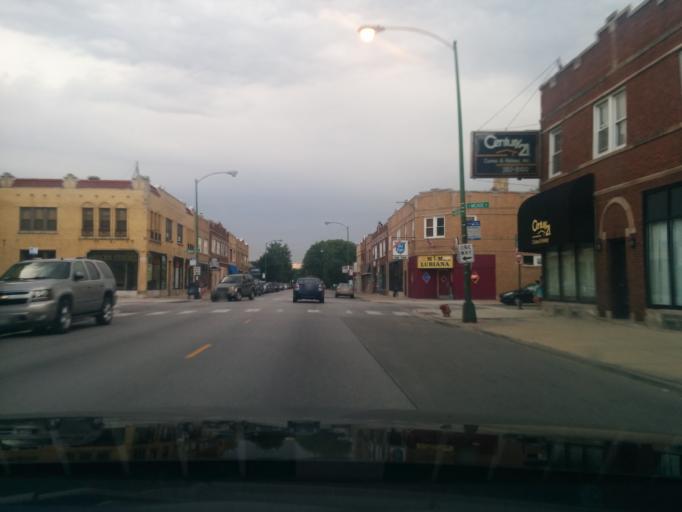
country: US
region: Illinois
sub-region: Cook County
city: Harwood Heights
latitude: 41.9458
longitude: -87.7784
